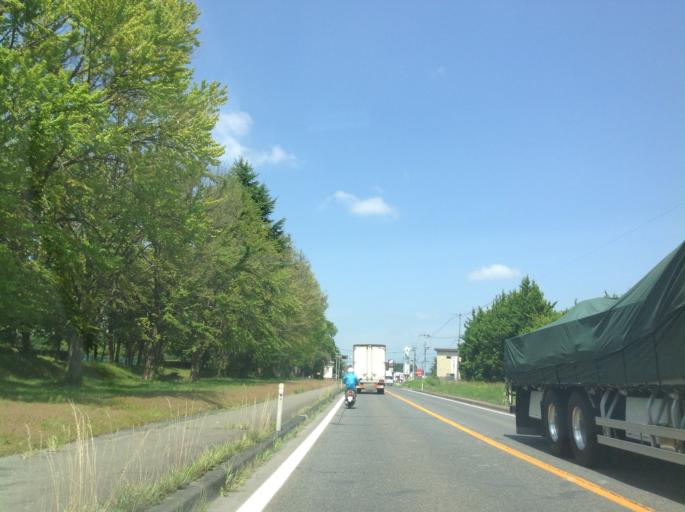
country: JP
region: Iwate
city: Hanamaki
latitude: 39.3528
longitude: 141.1102
